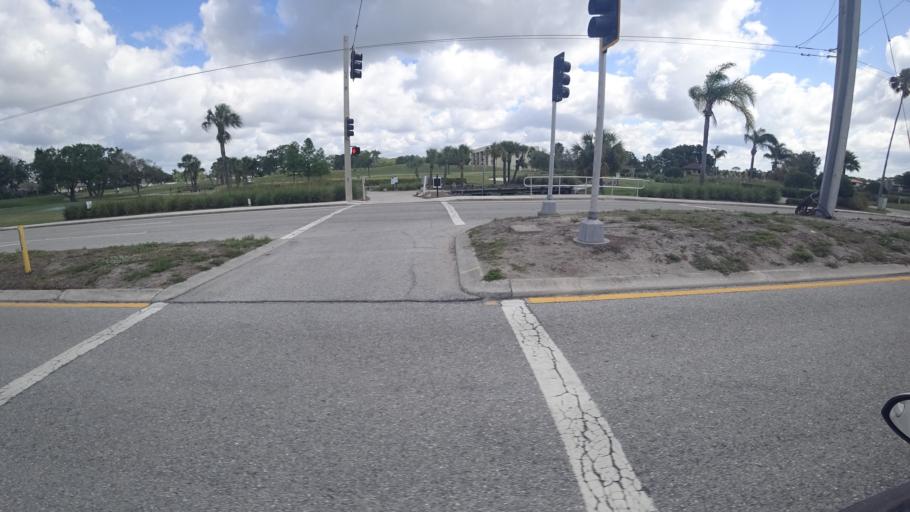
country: US
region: Florida
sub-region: Manatee County
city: Bayshore Gardens
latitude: 27.4292
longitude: -82.6051
